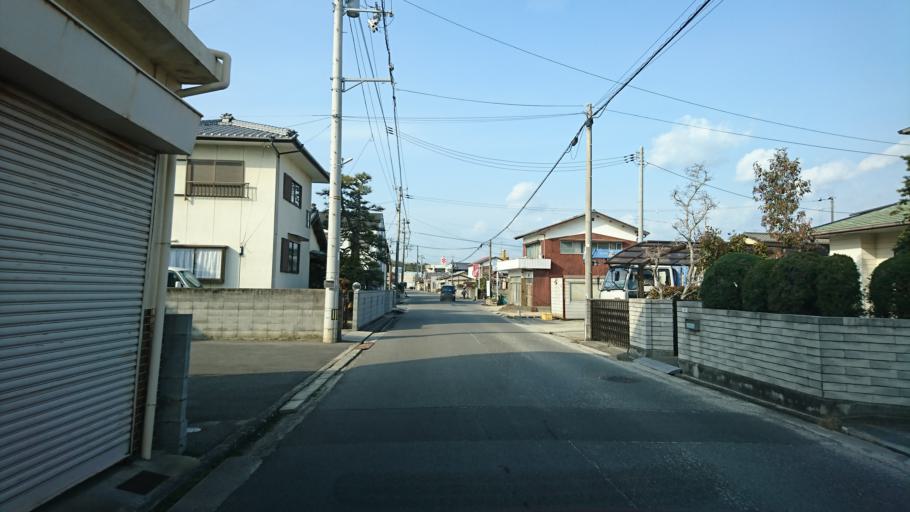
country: JP
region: Ehime
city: Saijo
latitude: 34.0233
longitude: 133.0391
